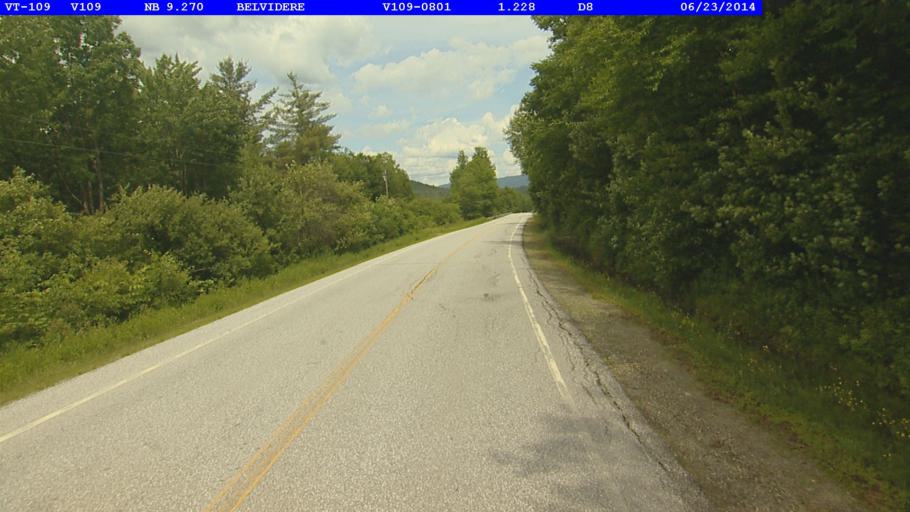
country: US
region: Vermont
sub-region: Lamoille County
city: Johnson
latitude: 44.7436
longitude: -72.7220
